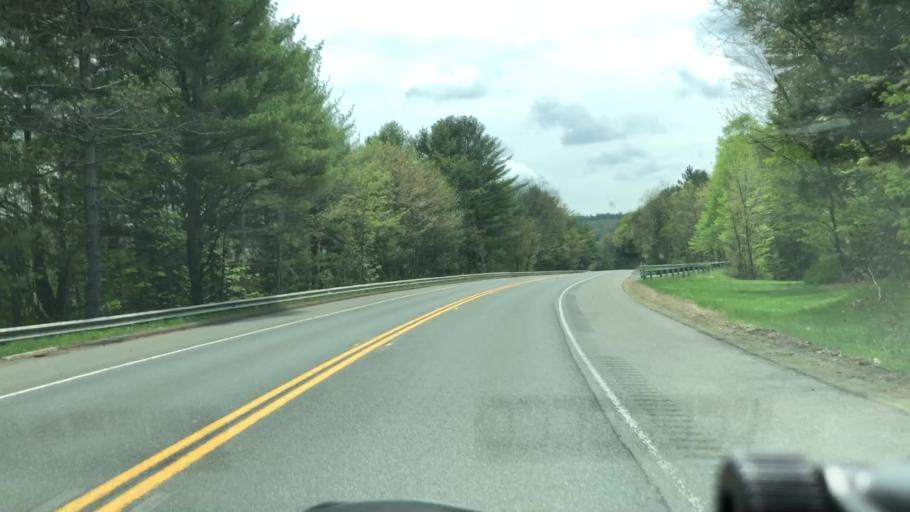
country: US
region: Massachusetts
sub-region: Hampshire County
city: Chesterfield
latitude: 42.4611
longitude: -72.8962
